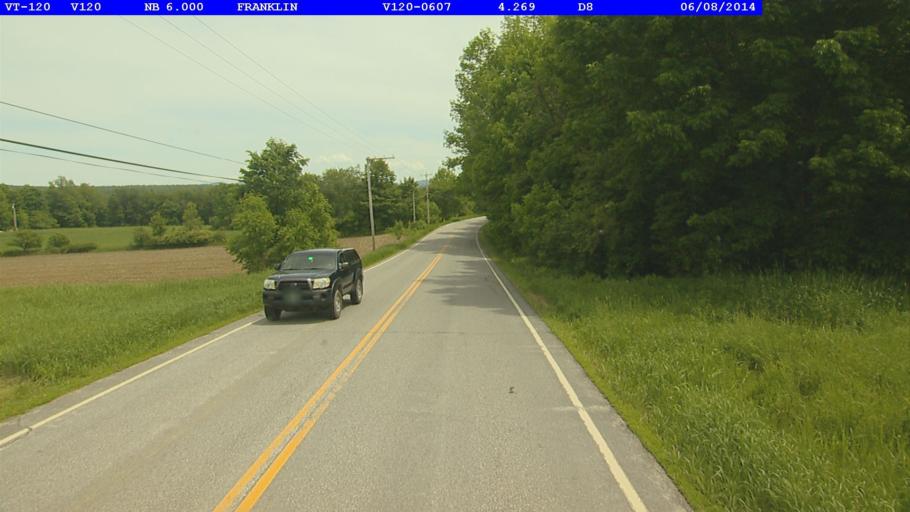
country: US
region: Vermont
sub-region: Franklin County
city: Enosburg Falls
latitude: 44.9871
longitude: -72.9081
